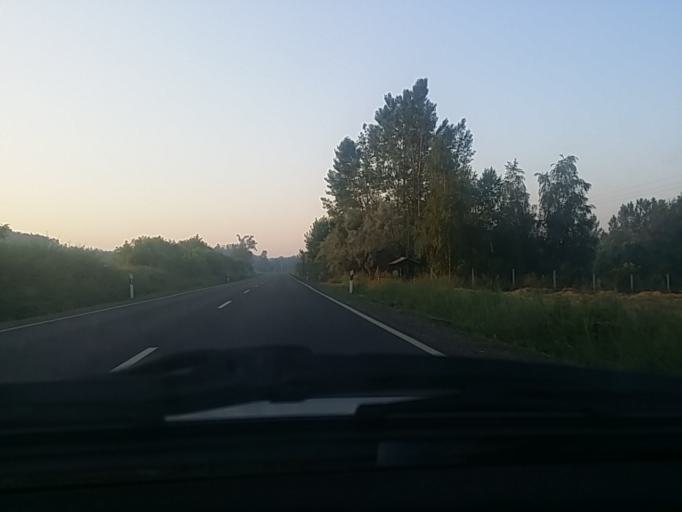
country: HU
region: Pest
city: Gyomro
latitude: 47.4434
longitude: 19.3984
